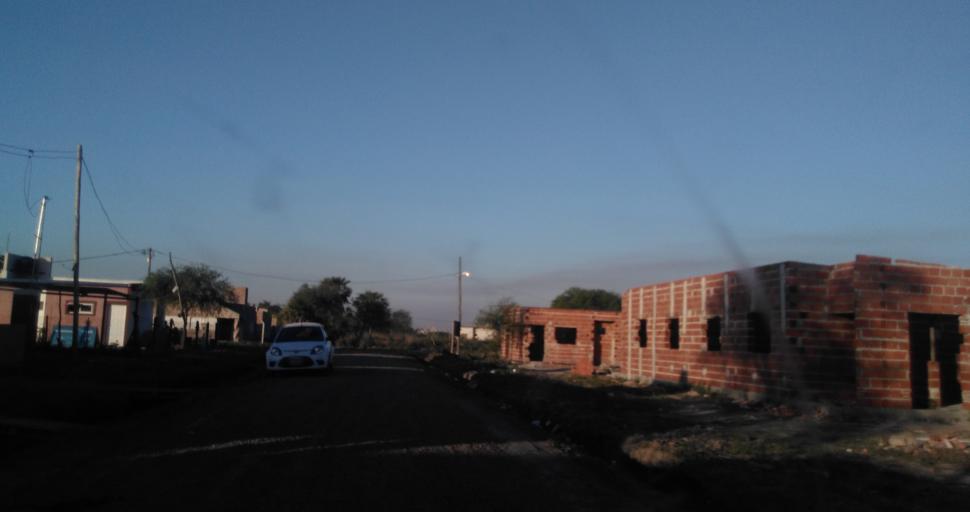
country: AR
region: Chaco
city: Resistencia
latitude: -27.4730
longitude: -59.0221
